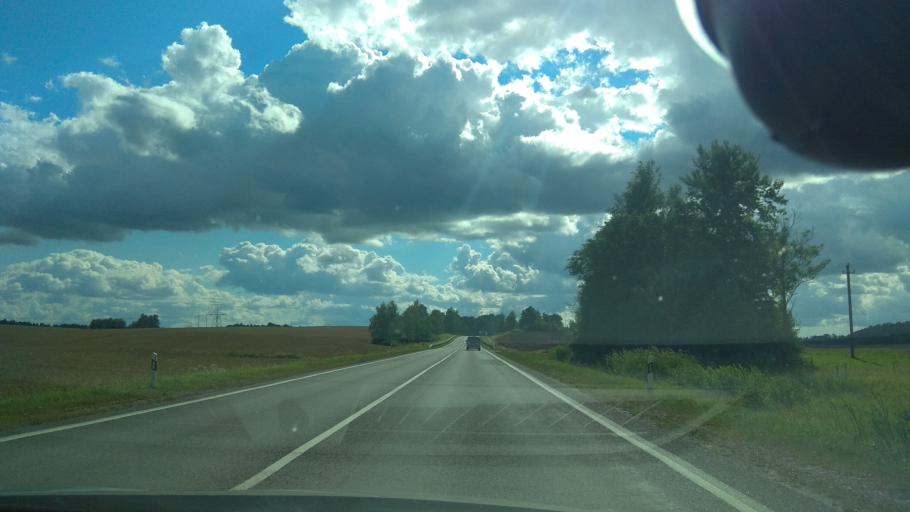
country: LT
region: Telsiu apskritis
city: Plunge
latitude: 55.9797
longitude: 22.0284
